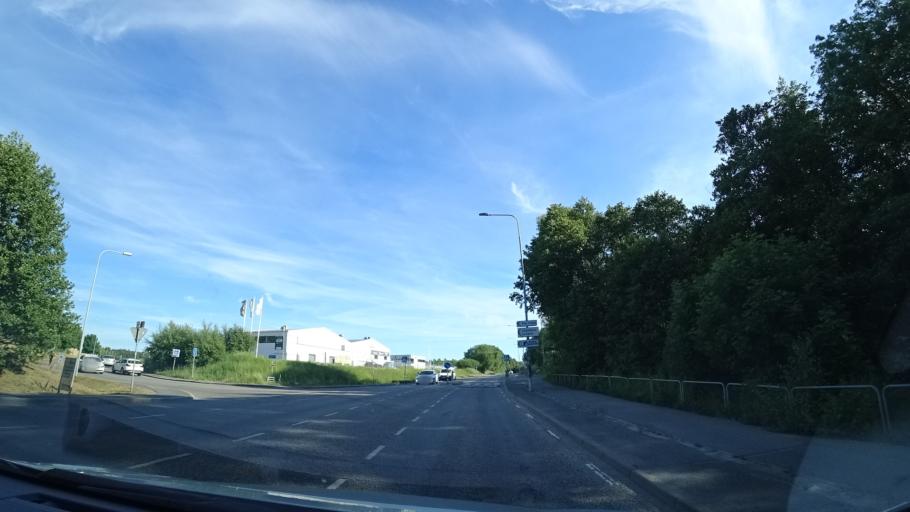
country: SE
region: Vaestra Goetaland
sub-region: Goteborg
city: Billdal
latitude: 57.5936
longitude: 11.9496
